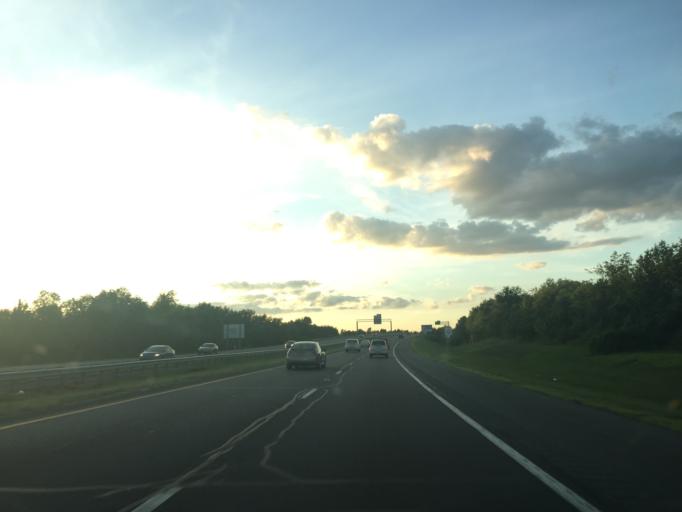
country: US
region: Delaware
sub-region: New Castle County
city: Bear
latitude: 39.6264
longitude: -75.6502
